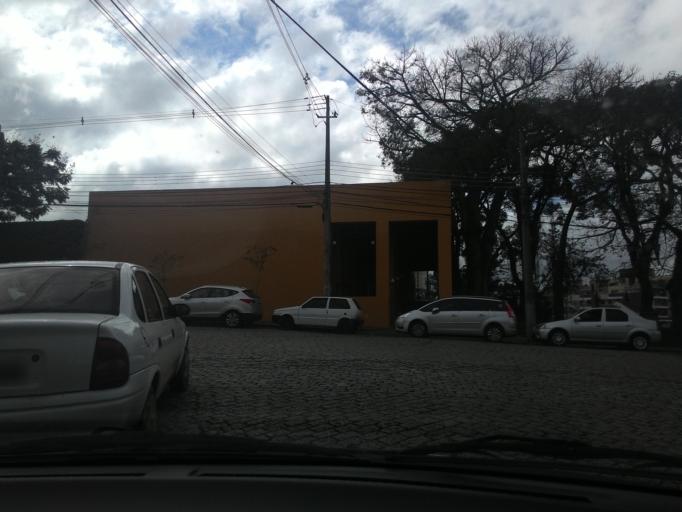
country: BR
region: Parana
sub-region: Curitiba
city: Curitiba
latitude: -25.4222
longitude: -49.2760
